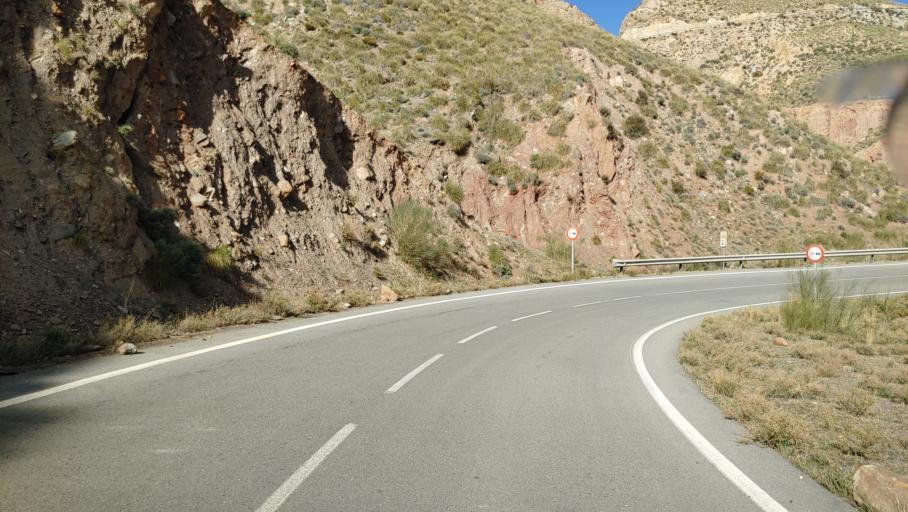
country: ES
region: Andalusia
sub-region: Provincia de Almeria
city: Canjayar
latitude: 37.0215
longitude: -2.7266
